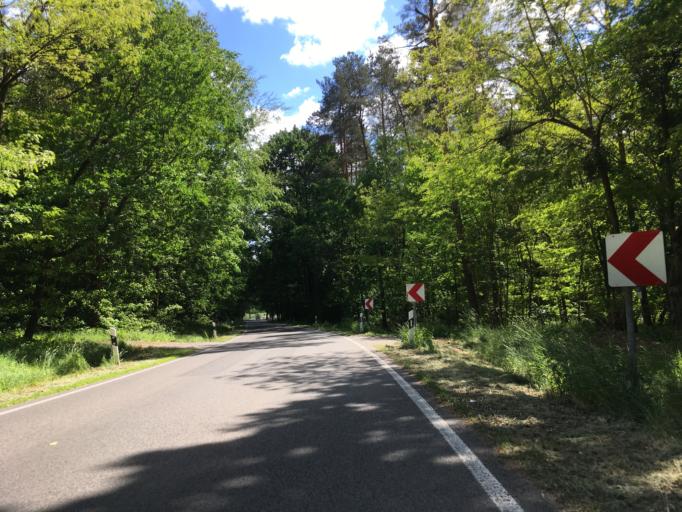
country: DE
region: Brandenburg
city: Protzel
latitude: 52.6617
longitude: 13.9890
